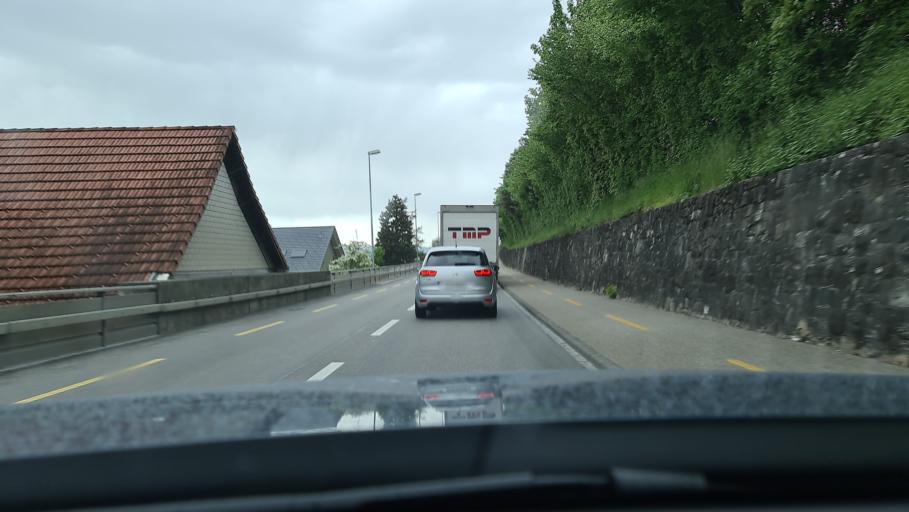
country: CH
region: Lucerne
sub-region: Sursee District
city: Bueron
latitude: 47.2147
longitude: 8.0932
